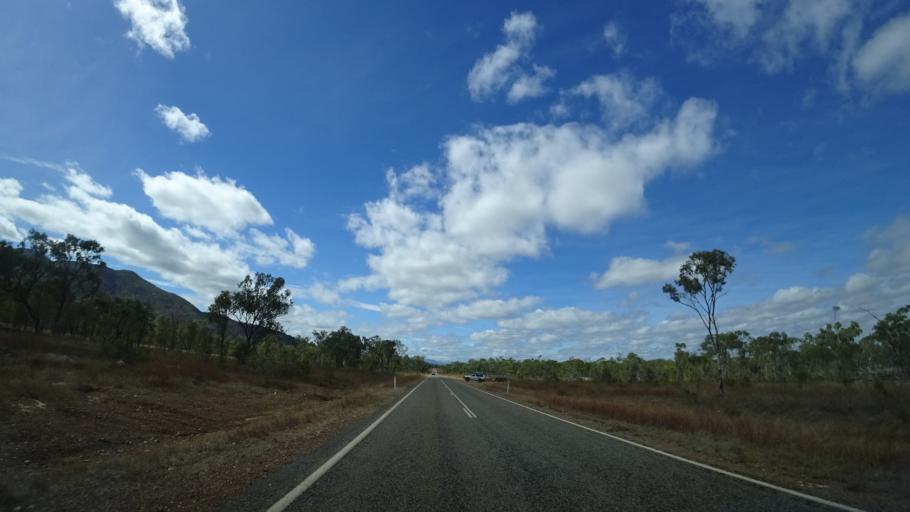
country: AU
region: Queensland
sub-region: Cairns
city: Port Douglas
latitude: -16.4852
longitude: 144.9001
